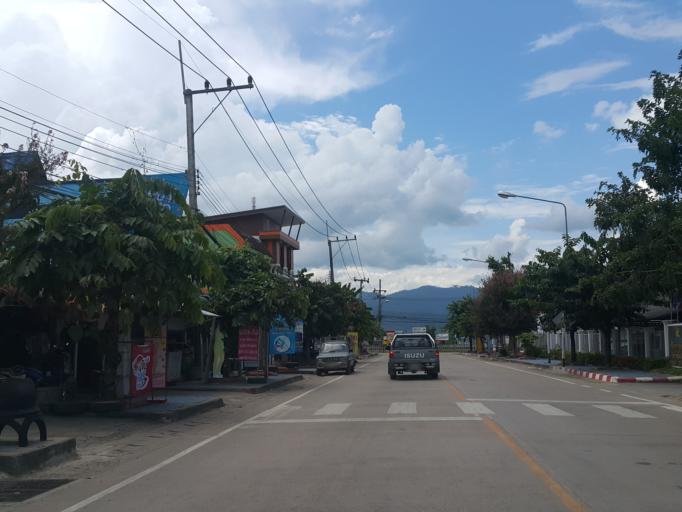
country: TH
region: Chiang Mai
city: Phrao
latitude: 19.3653
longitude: 99.2017
